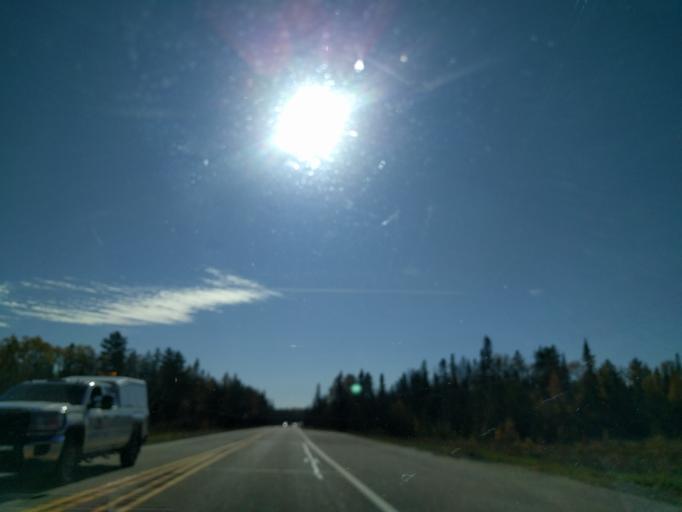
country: US
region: Michigan
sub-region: Marquette County
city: West Ishpeming
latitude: 46.4836
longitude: -87.9219
